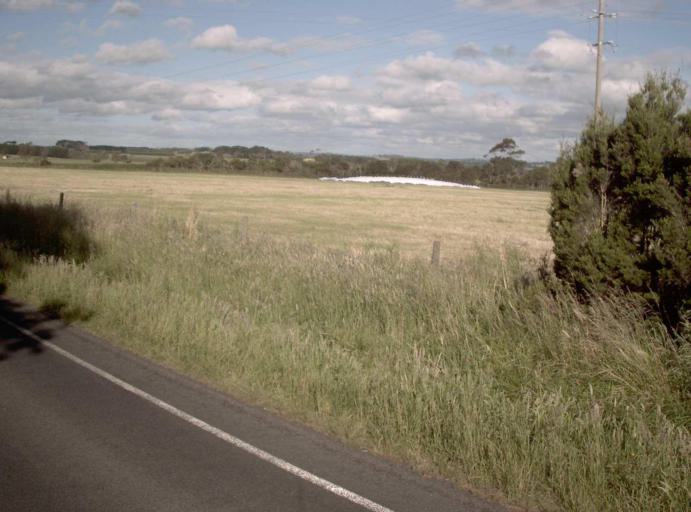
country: AU
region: Victoria
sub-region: Bass Coast
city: North Wonthaggi
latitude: -38.5057
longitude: 145.9119
